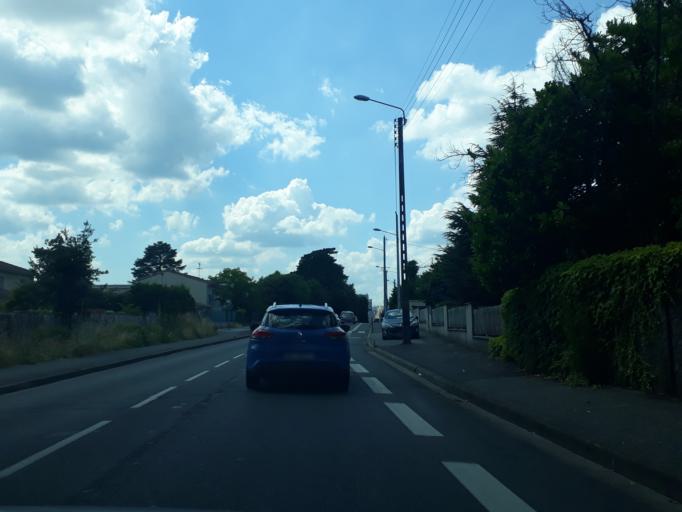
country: FR
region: Aquitaine
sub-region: Departement de la Gironde
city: Merignac
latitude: 44.8395
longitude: -0.6372
